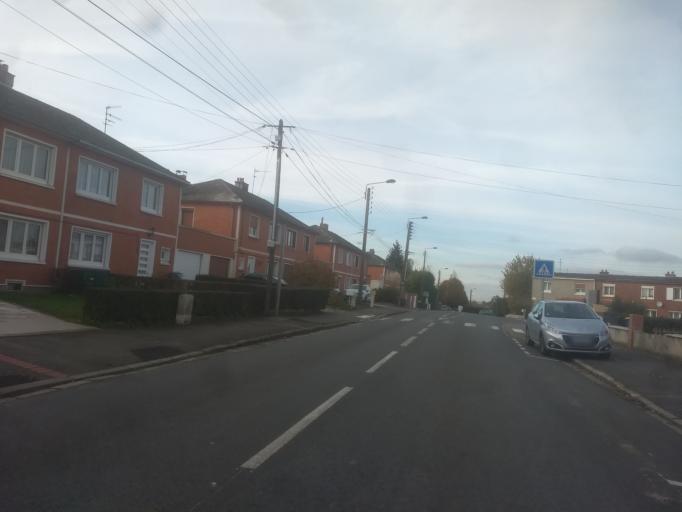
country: FR
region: Nord-Pas-de-Calais
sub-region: Departement du Pas-de-Calais
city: Beaurains
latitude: 50.2674
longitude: 2.7890
